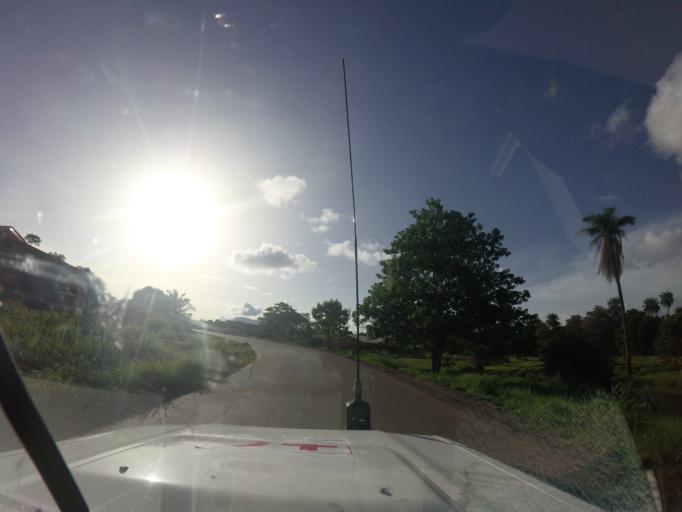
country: GN
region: Kindia
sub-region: Kindia
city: Kindia
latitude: 10.0191
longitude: -12.8287
